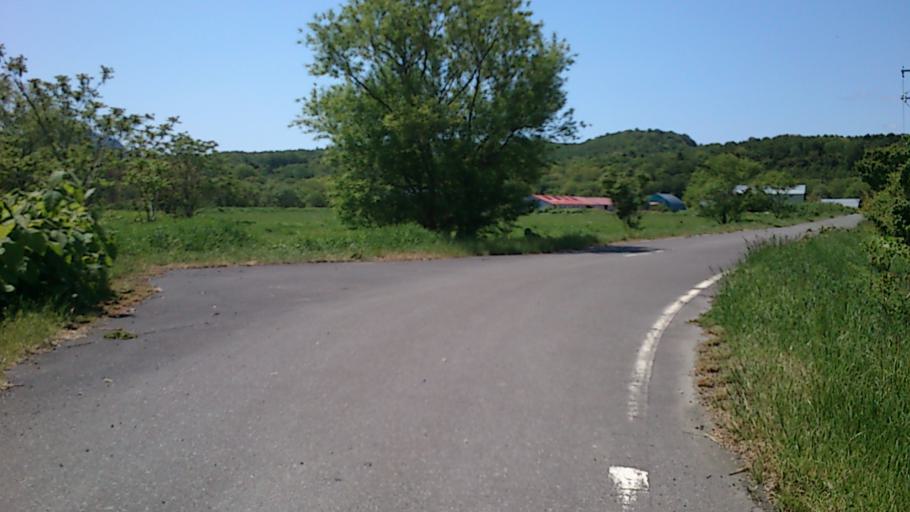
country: JP
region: Hokkaido
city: Makubetsu
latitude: 45.0527
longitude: 142.3556
